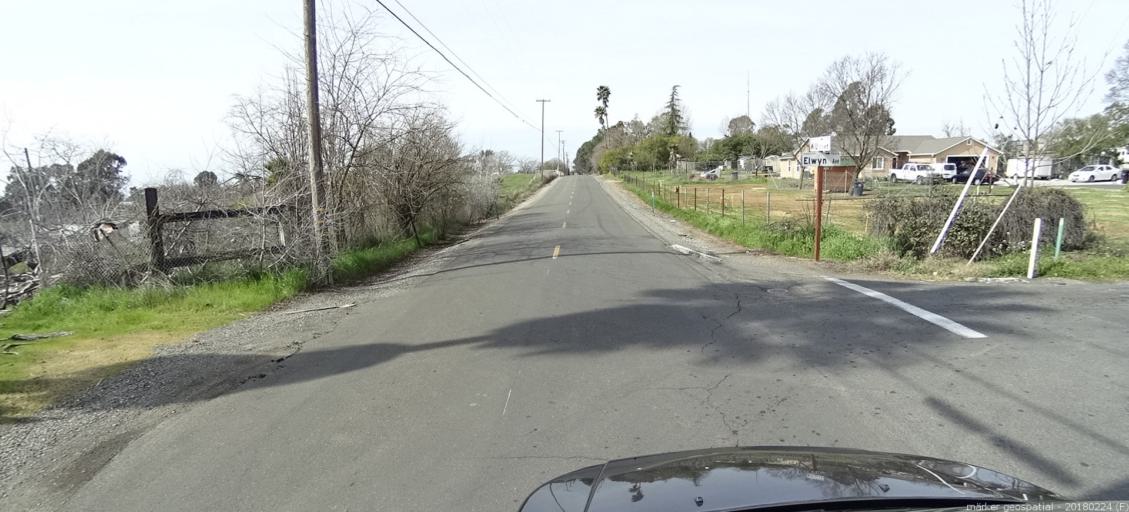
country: US
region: California
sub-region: Sacramento County
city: Elverta
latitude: 38.7052
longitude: -121.4665
